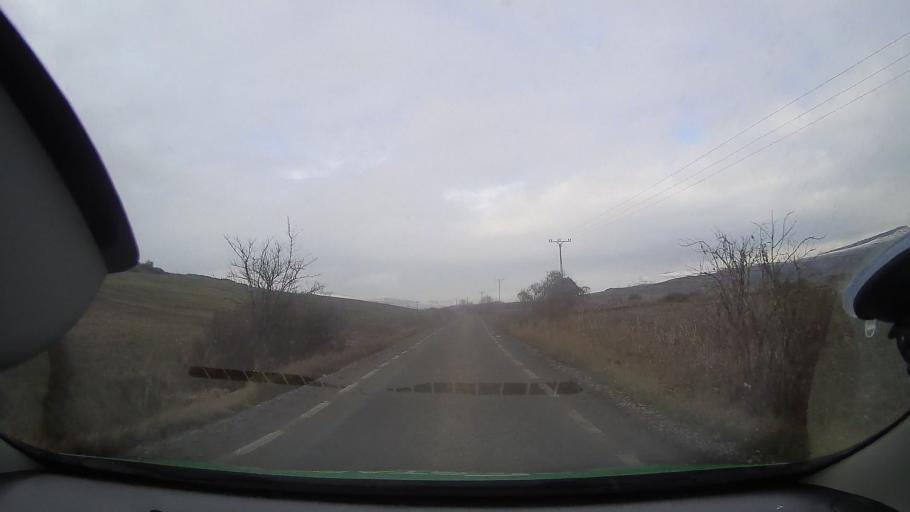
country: RO
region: Mures
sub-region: Comuna Atintis
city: Atintis
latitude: 46.4009
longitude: 24.0888
